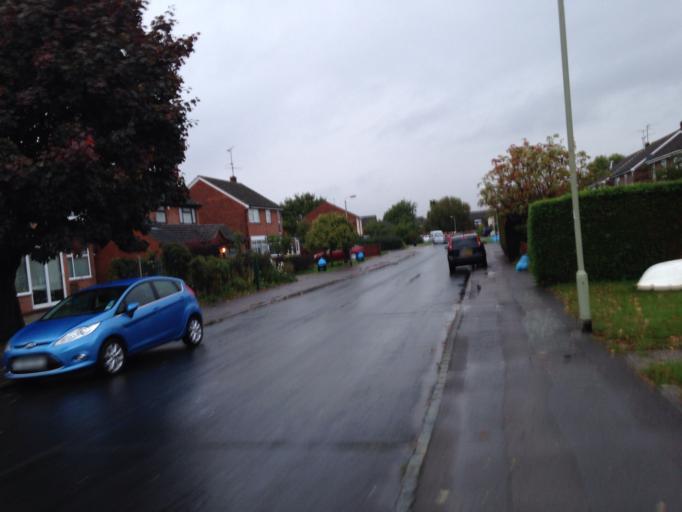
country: GB
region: England
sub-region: Wokingham
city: Winnersh
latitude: 51.4313
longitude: -0.8855
